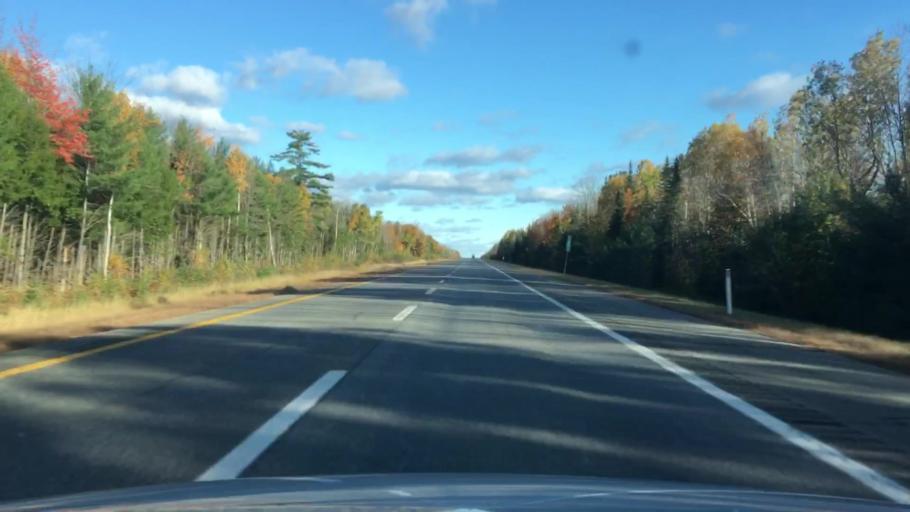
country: US
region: Maine
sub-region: Penobscot County
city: Greenbush
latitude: 45.0730
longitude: -68.6908
